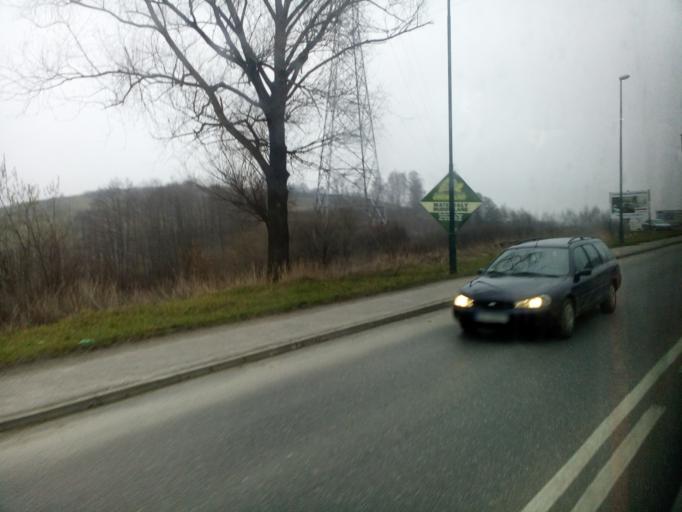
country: PL
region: Lesser Poland Voivodeship
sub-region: Powiat nowosadecki
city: Stary Sacz
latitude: 49.5752
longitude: 20.6634
